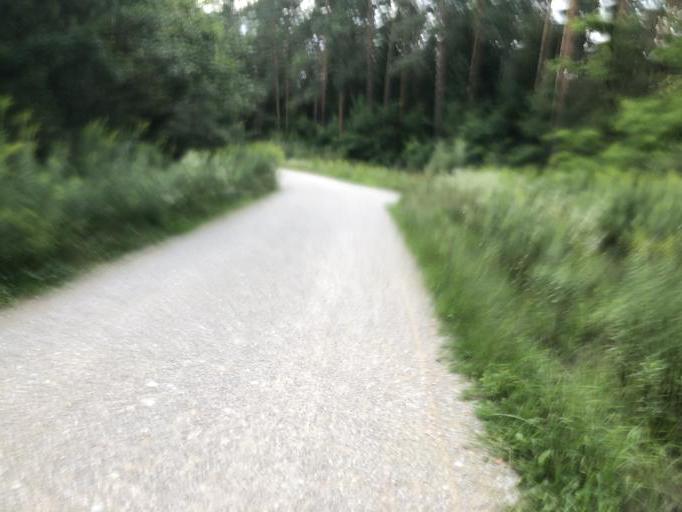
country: DE
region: Bavaria
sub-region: Regierungsbezirk Mittelfranken
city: Buckenhof
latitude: 49.5869
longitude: 11.0412
